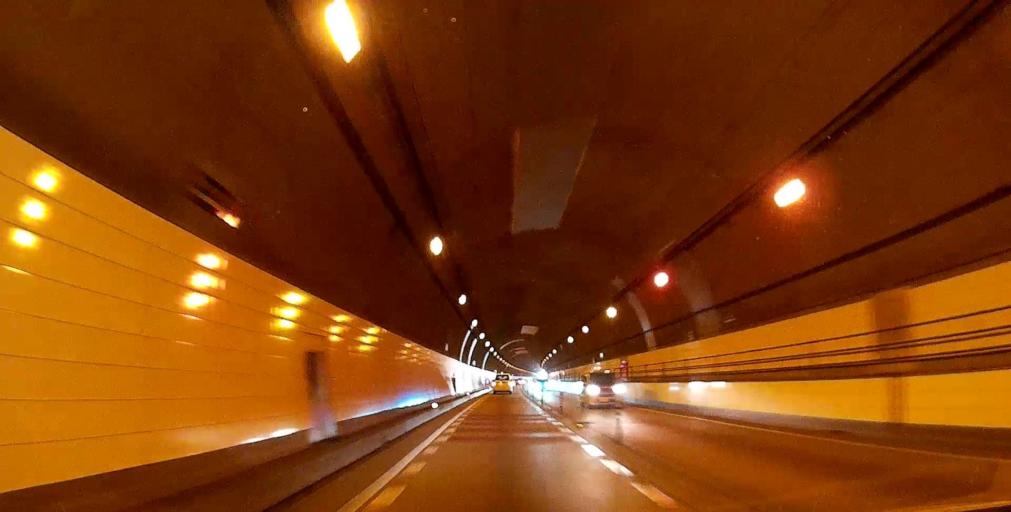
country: JP
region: Yamanashi
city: Isawa
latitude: 35.6645
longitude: 138.6245
